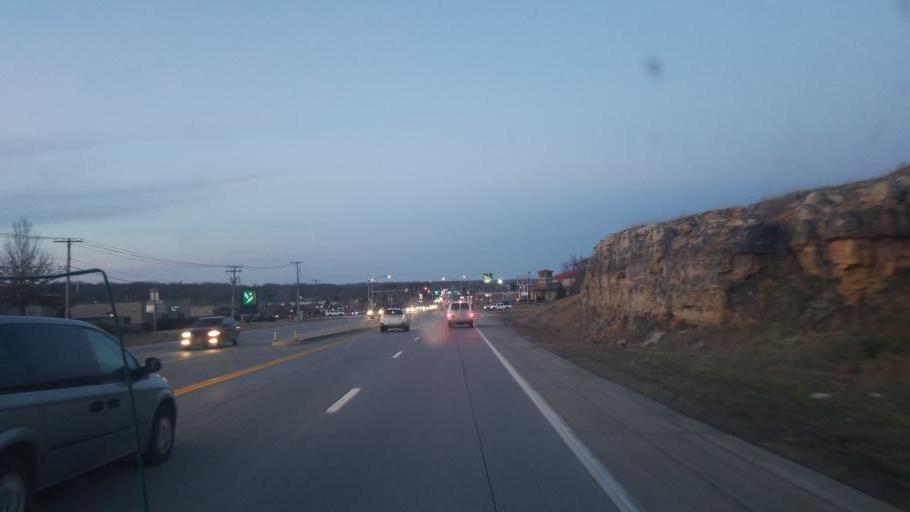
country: US
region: Missouri
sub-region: Howell County
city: West Plains
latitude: 36.7241
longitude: -91.8774
